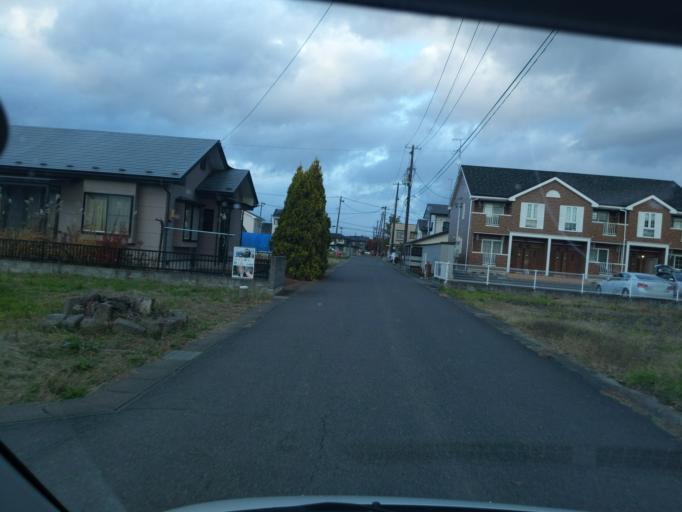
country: JP
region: Iwate
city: Mizusawa
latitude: 39.0493
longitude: 141.1271
